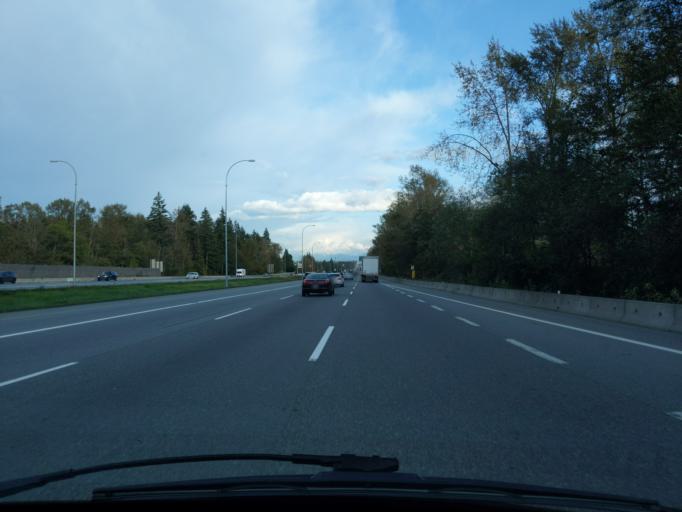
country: CA
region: British Columbia
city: Pitt Meadows
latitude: 49.1787
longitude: -122.7249
